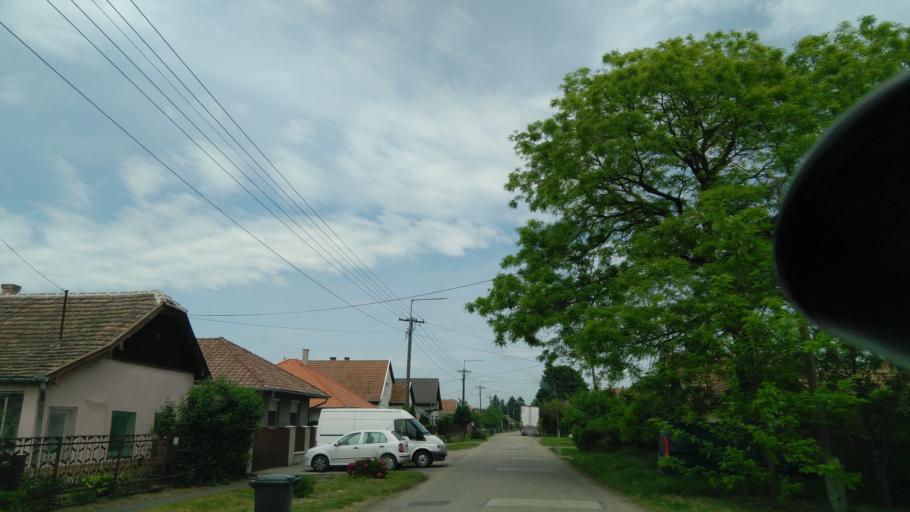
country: HU
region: Bekes
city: Fuzesgyarmat
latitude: 47.1022
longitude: 21.2055
